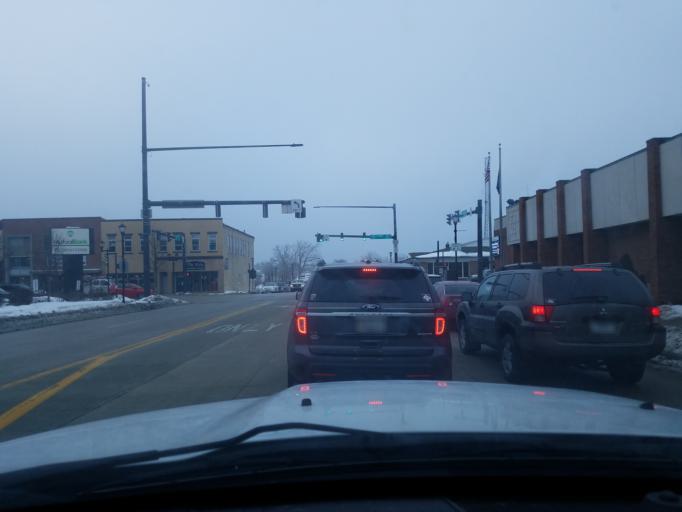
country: US
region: Indiana
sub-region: Saint Joseph County
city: Mishawaka
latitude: 41.6607
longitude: -86.1792
